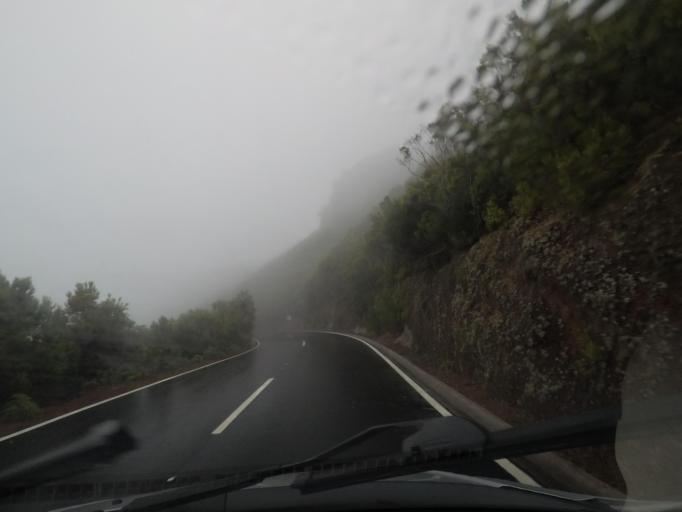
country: PT
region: Madeira
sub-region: Santana
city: Santana
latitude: 32.7666
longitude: -16.9215
